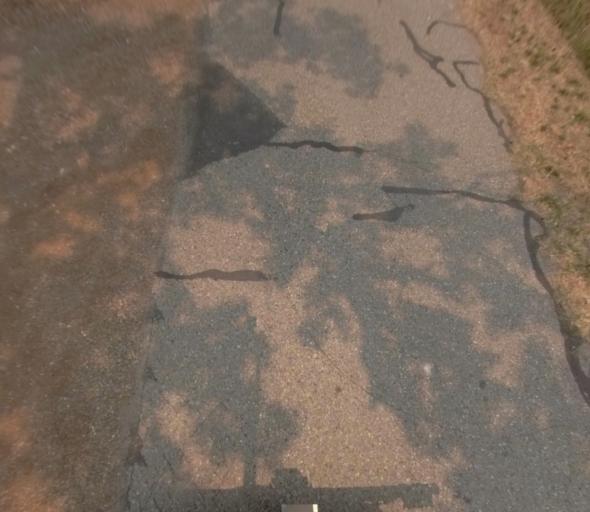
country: US
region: California
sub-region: Madera County
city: Oakhurst
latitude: 37.2903
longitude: -119.6543
